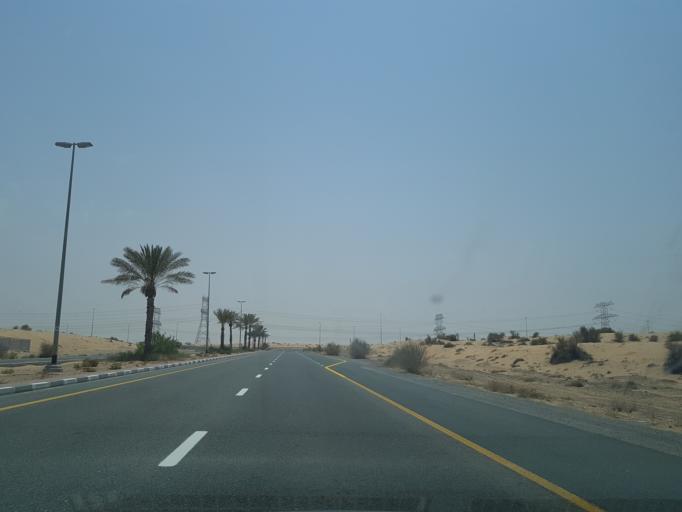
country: AE
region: Ash Shariqah
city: Sharjah
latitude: 25.1056
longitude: 55.4124
